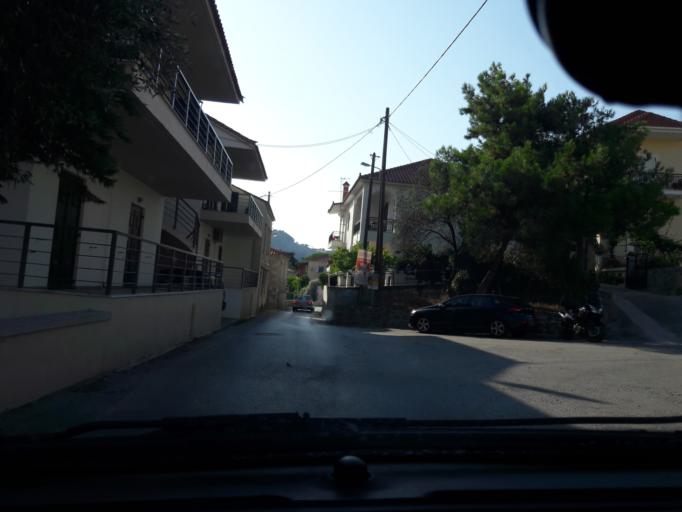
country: GR
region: North Aegean
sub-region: Nomos Lesvou
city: Myrina
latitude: 39.8721
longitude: 25.0664
